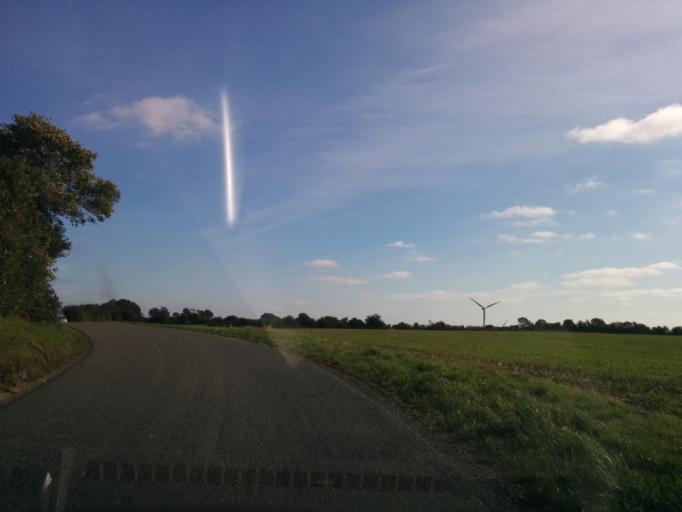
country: DK
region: South Denmark
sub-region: Kolding Kommune
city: Sonder Bjert
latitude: 55.4040
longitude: 9.5554
